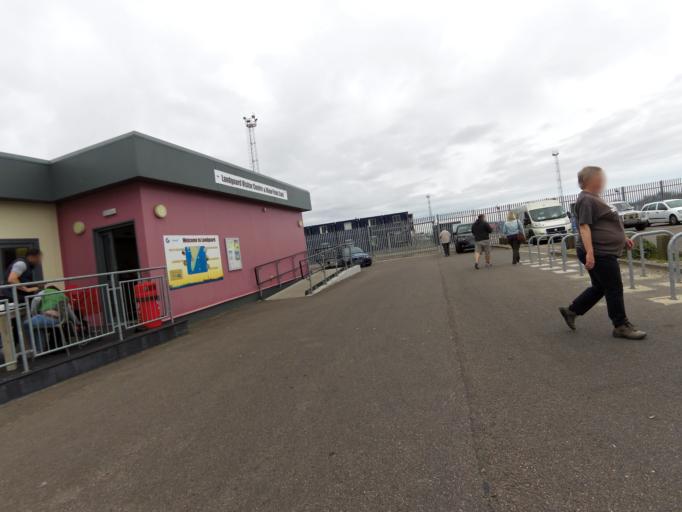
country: GB
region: England
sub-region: Essex
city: Harwich
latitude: 51.9404
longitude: 1.3201
